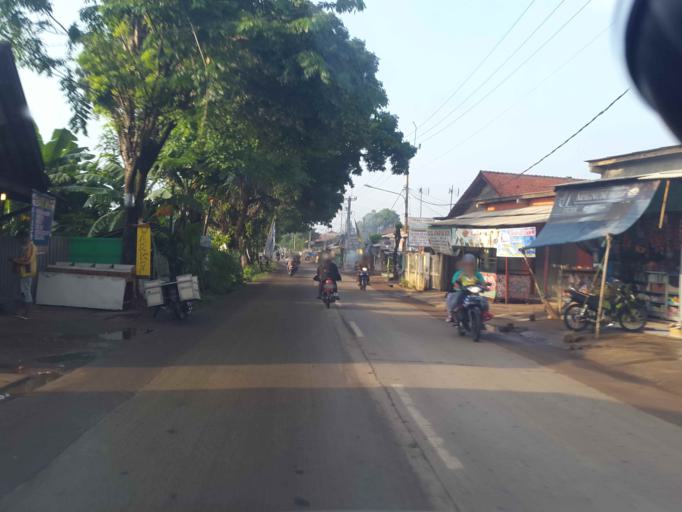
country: ID
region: West Java
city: Cikarang
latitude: -6.2843
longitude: 107.0717
